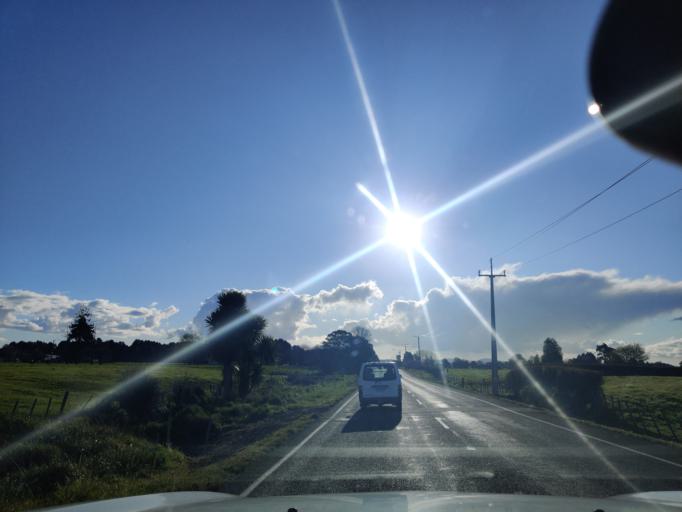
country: NZ
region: Waikato
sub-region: Hamilton City
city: Hamilton
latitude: -37.6856
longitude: 175.3320
